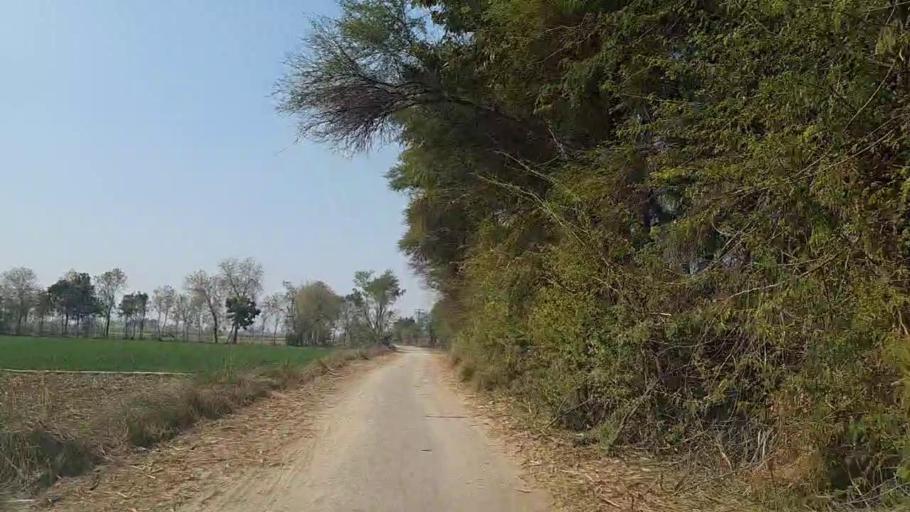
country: PK
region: Sindh
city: Daur
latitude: 26.5032
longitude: 68.3243
